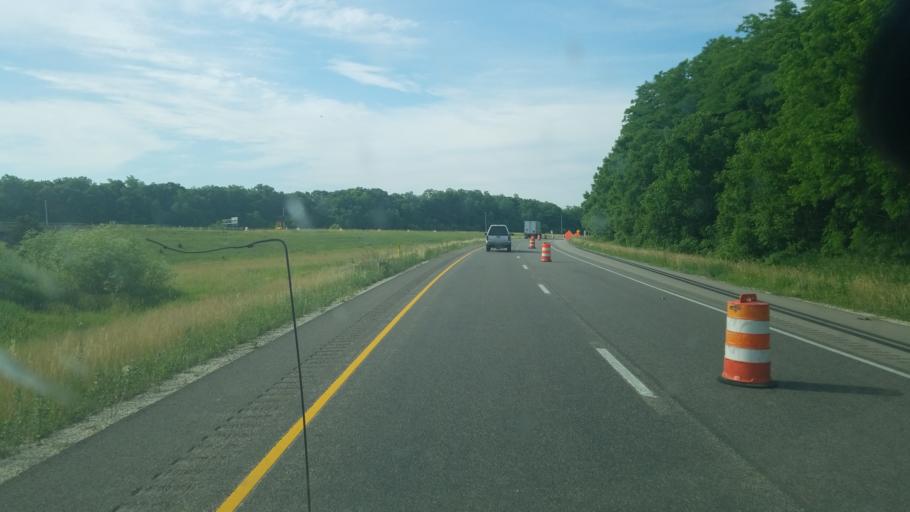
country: US
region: Illinois
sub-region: Peoria County
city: Bellevue
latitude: 40.7391
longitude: -89.6711
